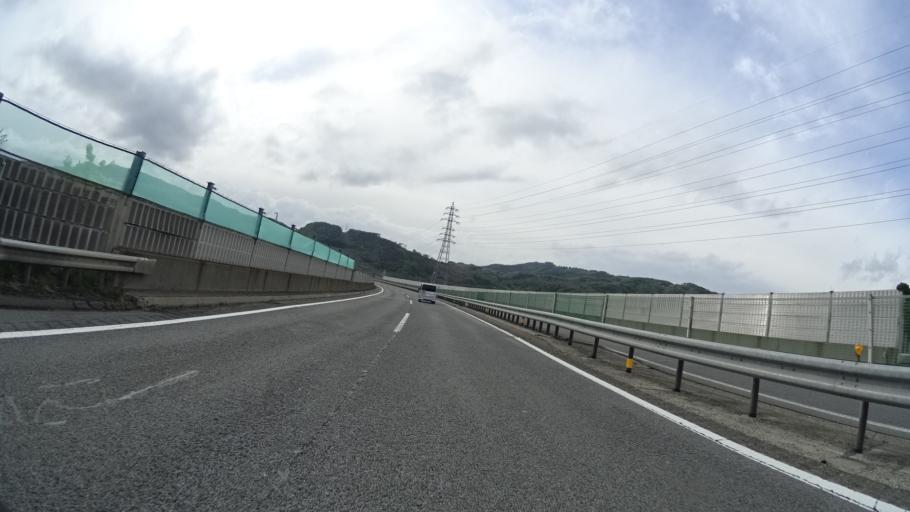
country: JP
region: Nagano
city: Nagano-shi
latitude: 36.5574
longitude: 138.1197
